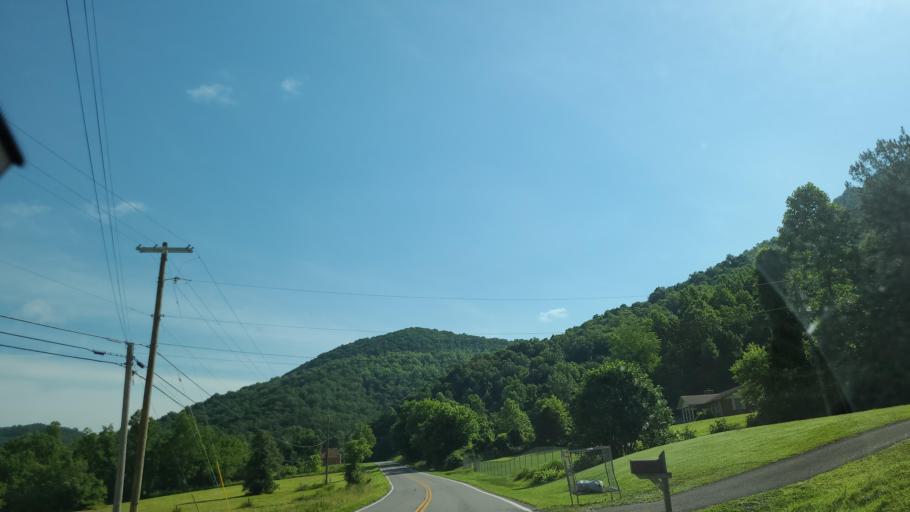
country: US
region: Kentucky
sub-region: Bell County
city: Pineville
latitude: 36.7669
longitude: -83.7740
